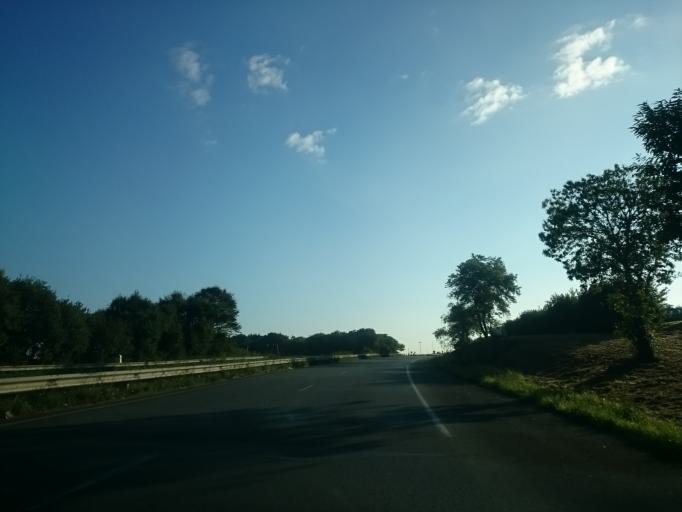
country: FR
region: Brittany
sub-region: Departement du Finistere
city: Gouesnou
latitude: 48.4305
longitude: -4.4728
